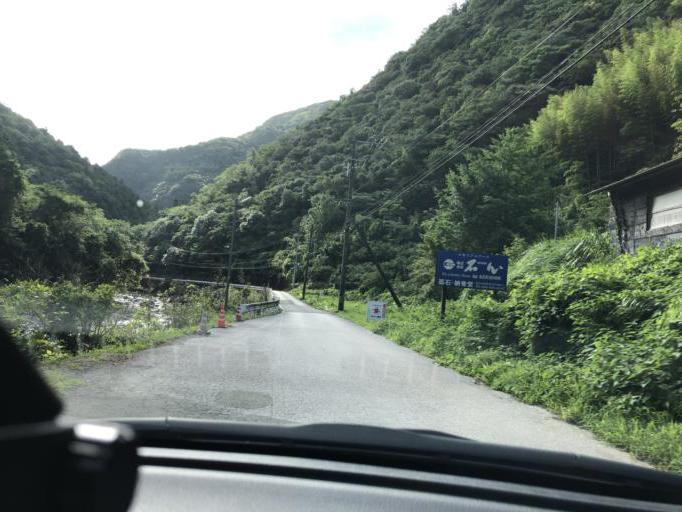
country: JP
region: Kochi
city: Kochi-shi
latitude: 33.6283
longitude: 133.5125
